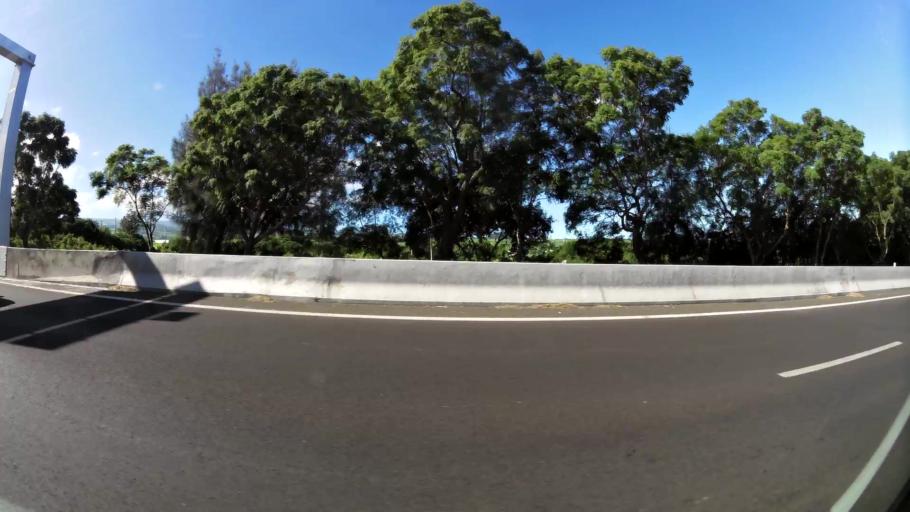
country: RE
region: Reunion
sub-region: Reunion
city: Le Tampon
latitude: -21.2913
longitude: 55.5135
